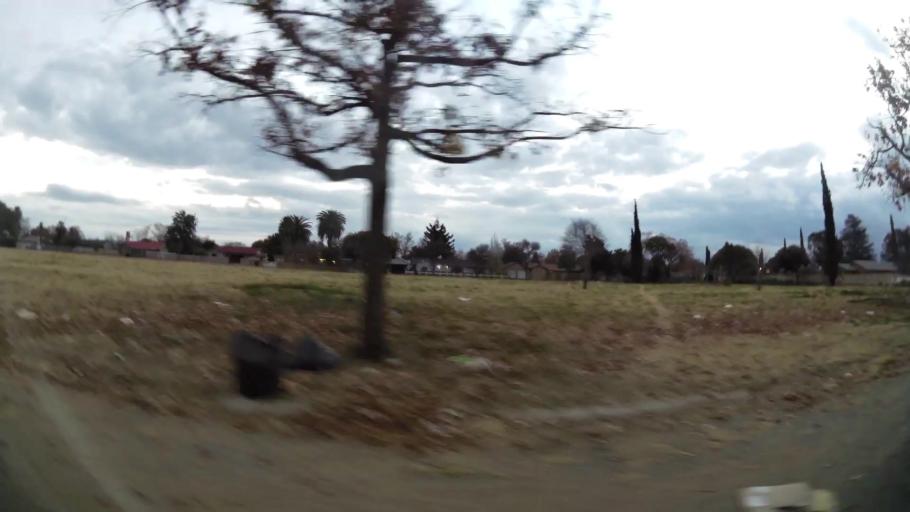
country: ZA
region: Orange Free State
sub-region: Lejweleputswa District Municipality
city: Welkom
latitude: -27.9782
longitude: 26.7496
